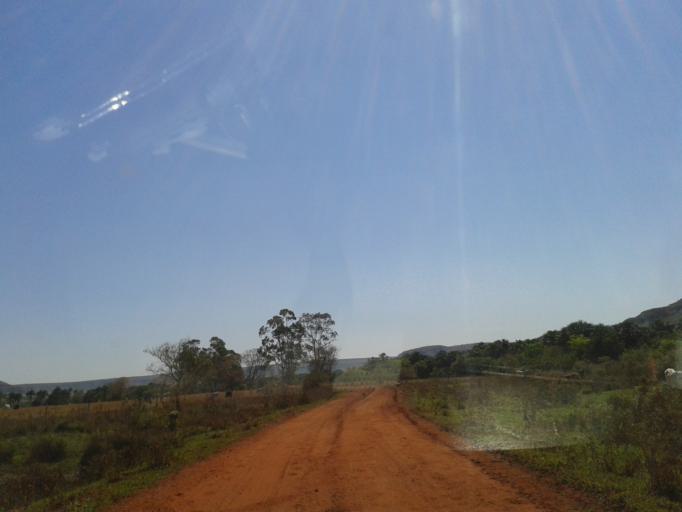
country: BR
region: Minas Gerais
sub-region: Santa Vitoria
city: Santa Vitoria
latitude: -19.0684
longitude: -50.0477
